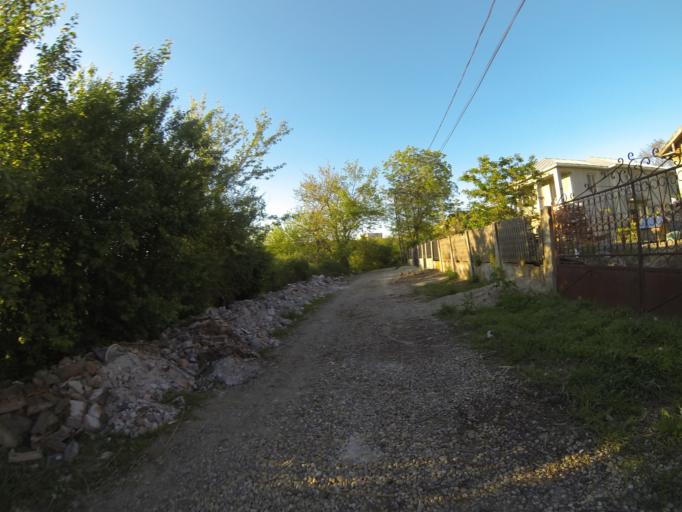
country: RO
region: Dolj
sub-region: Comuna Segarcea
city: Segarcea
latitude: 44.0946
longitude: 23.7446
